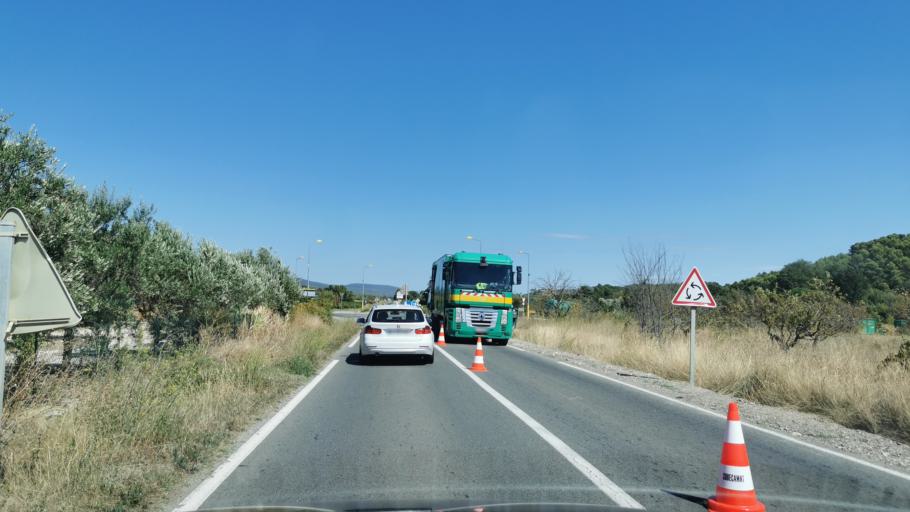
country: FR
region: Languedoc-Roussillon
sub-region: Departement de l'Aude
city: Conques-sur-Orbiel
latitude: 43.2900
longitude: 2.4440
